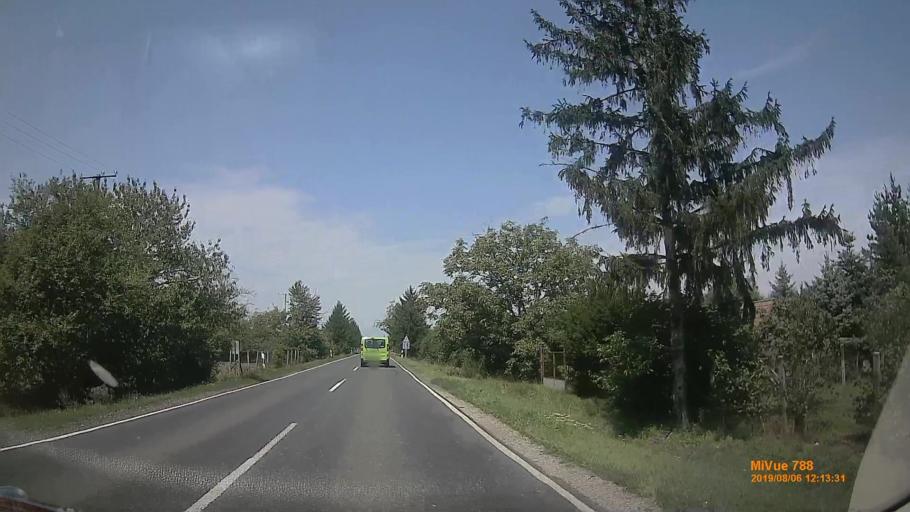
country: HU
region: Vas
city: Vasvar
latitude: 47.1317
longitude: 16.8408
